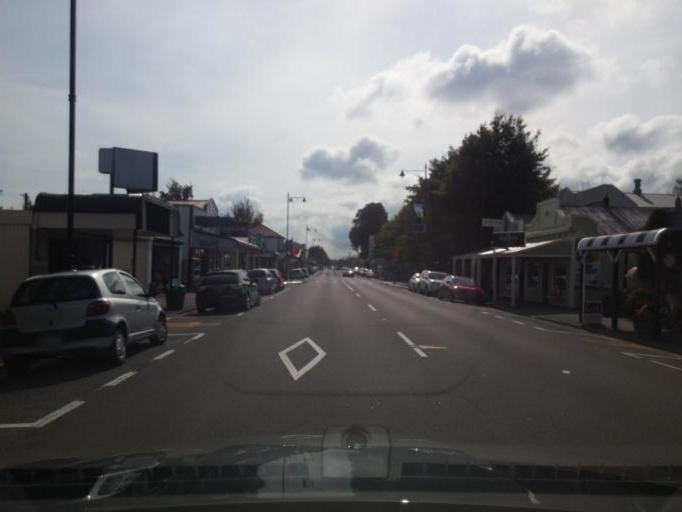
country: NZ
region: Wellington
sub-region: Masterton District
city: Masterton
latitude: -41.0804
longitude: 175.4603
